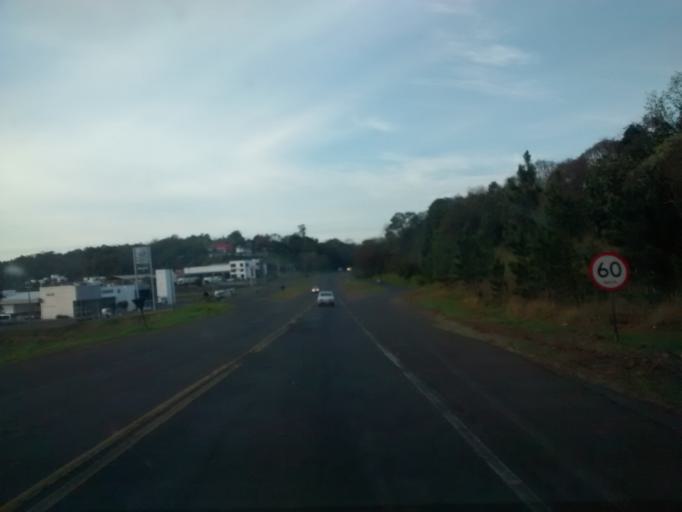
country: BR
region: Parana
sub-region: Francisco Beltrao
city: Francisco Beltrao
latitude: -26.1009
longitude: -53.0591
